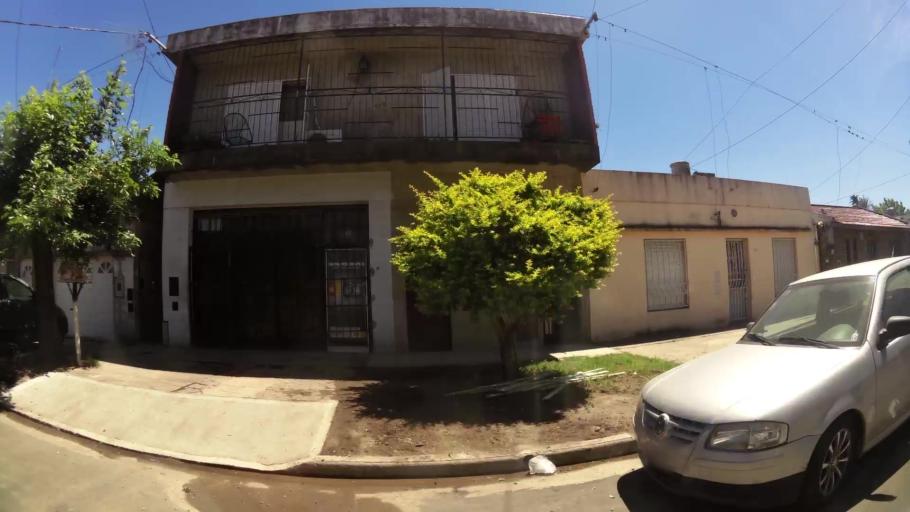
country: AR
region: Santa Fe
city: Perez
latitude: -32.9498
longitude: -60.7141
